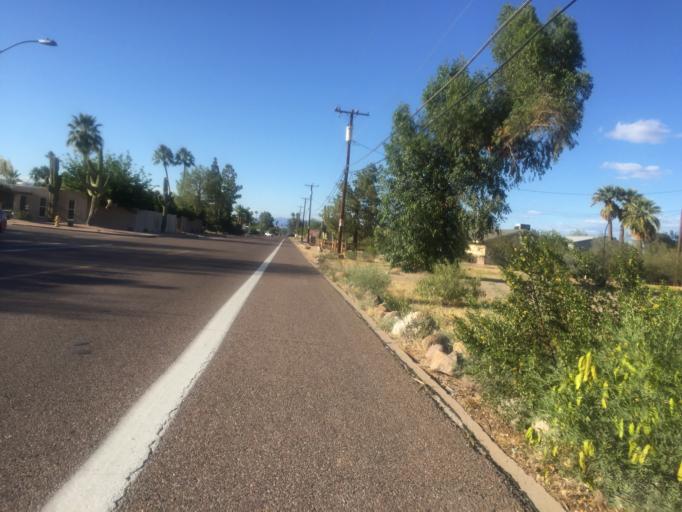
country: US
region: Arizona
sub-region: Maricopa County
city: Paradise Valley
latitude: 33.5795
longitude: -112.0044
